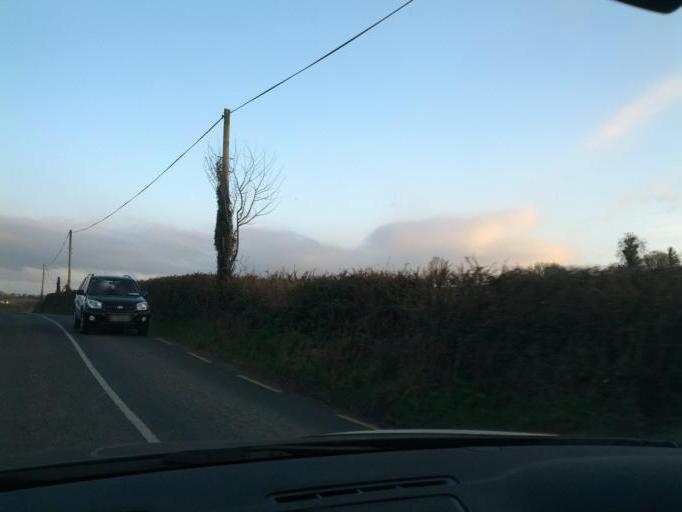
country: IE
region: Munster
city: Nenagh Bridge
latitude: 52.9527
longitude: -8.2314
